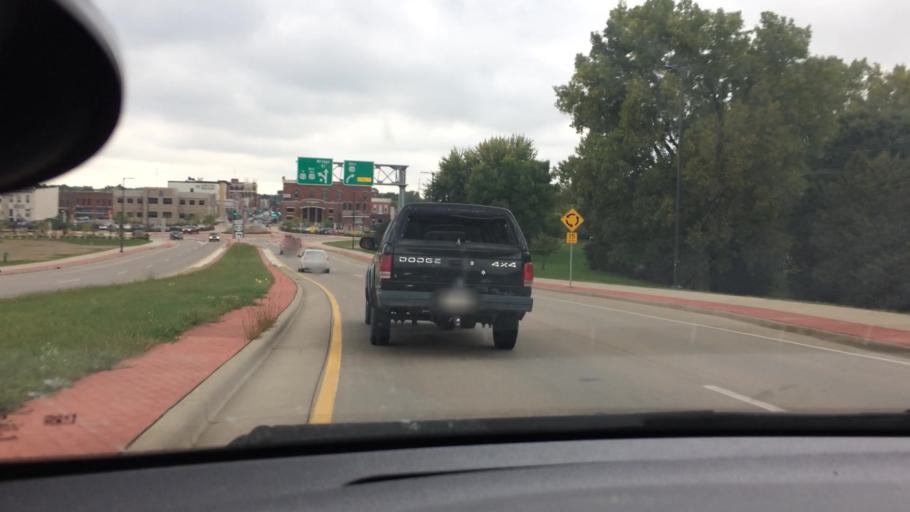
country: US
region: Wisconsin
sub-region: Chippewa County
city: Chippewa Falls
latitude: 44.9336
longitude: -91.3888
